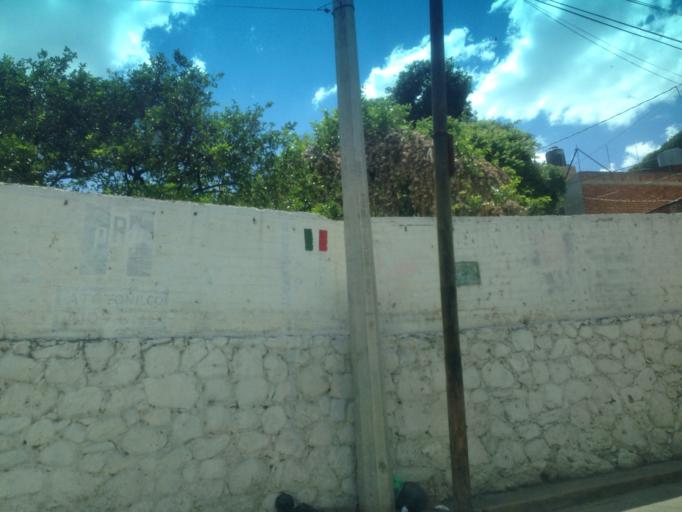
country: MX
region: Jalisco
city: Atotonilco el Alto
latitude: 20.5545
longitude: -102.5105
